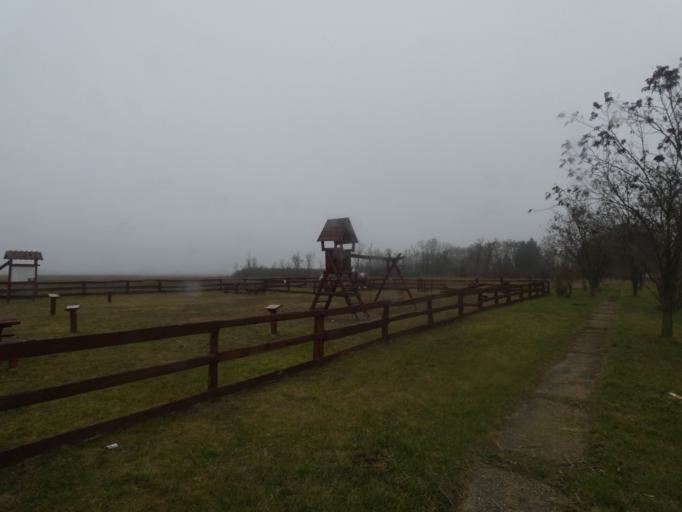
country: HU
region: Pest
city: Tapiogyorgye
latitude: 47.3002
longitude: 19.9821
